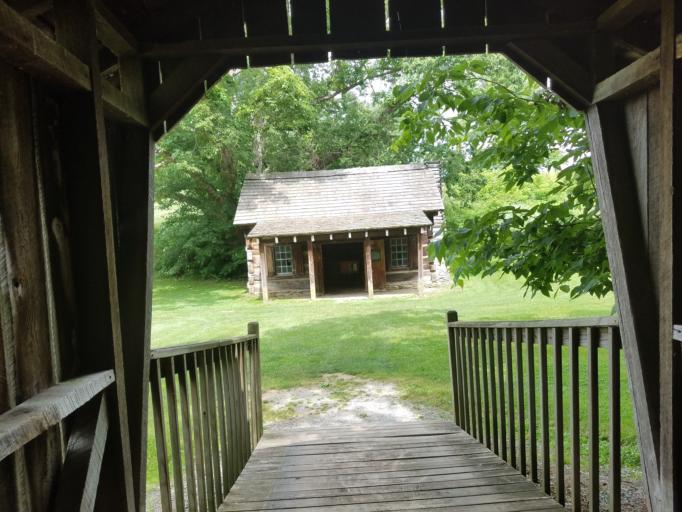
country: US
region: Kentucky
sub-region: Washington County
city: Springfield
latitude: 37.7607
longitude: -85.2149
